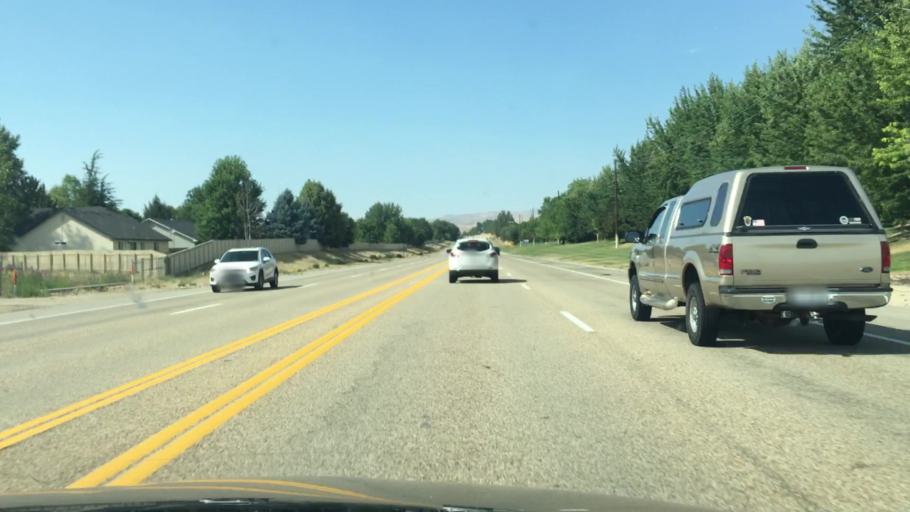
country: US
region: Idaho
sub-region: Ada County
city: Eagle
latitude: 43.7008
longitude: -116.3191
